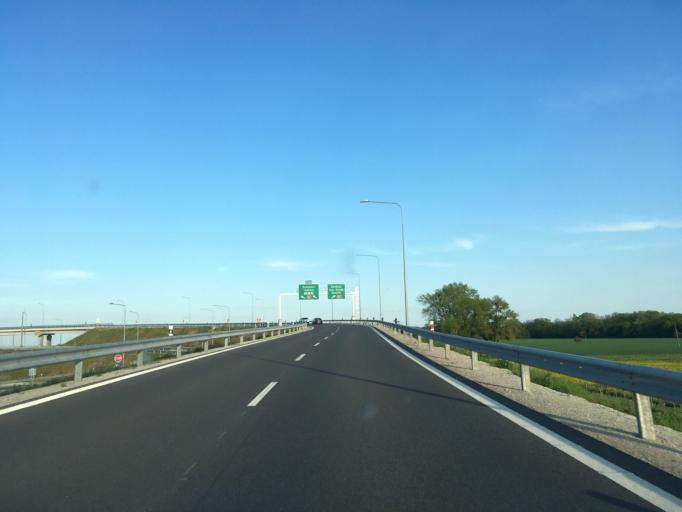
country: SK
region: Bratislavsky
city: Dunajska Luzna
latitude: 48.0896
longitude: 17.1838
